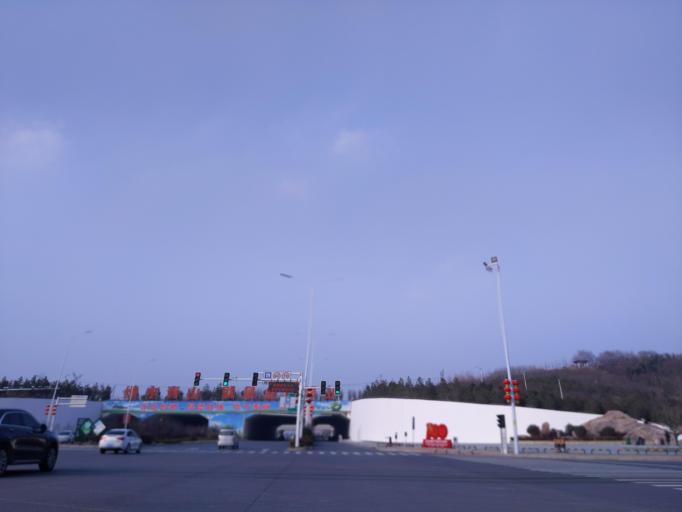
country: CN
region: Henan Sheng
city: Puyang
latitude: 35.8173
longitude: 115.0227
